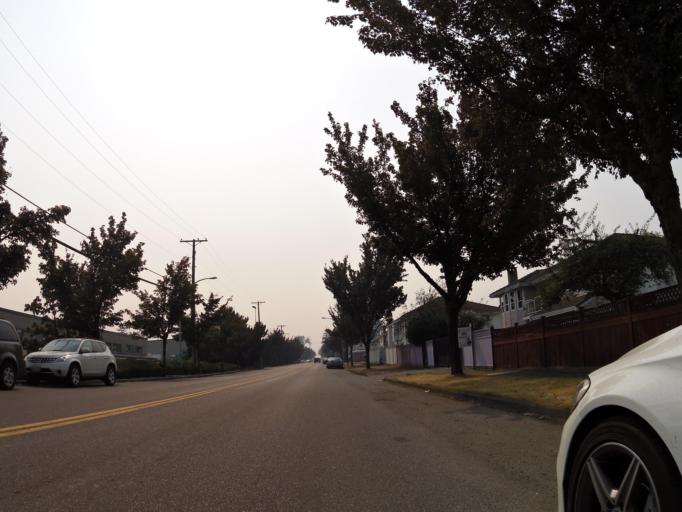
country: CA
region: British Columbia
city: Delta
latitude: 49.1510
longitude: -122.8791
